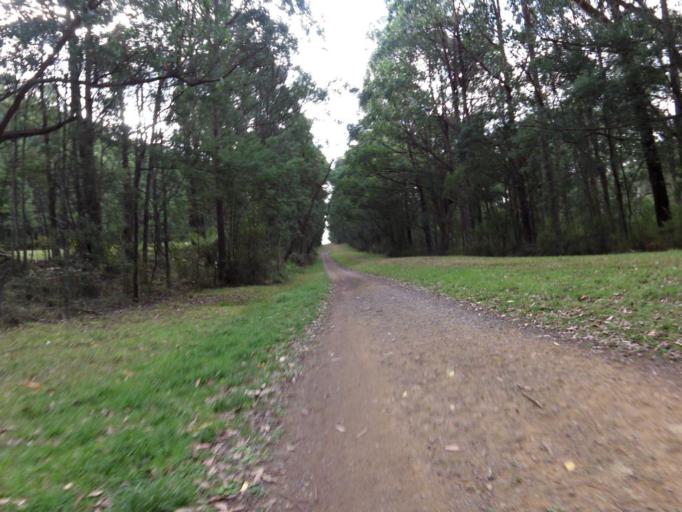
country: AU
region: Victoria
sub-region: Yarra Ranges
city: Mount Evelyn
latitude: -37.8096
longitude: 145.3949
